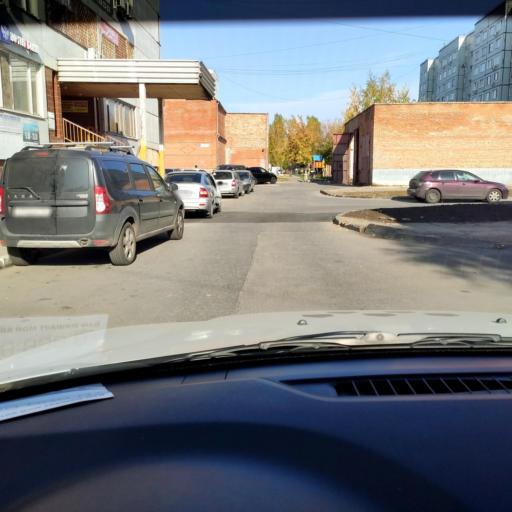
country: RU
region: Samara
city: Tol'yatti
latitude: 53.5059
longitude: 49.4307
